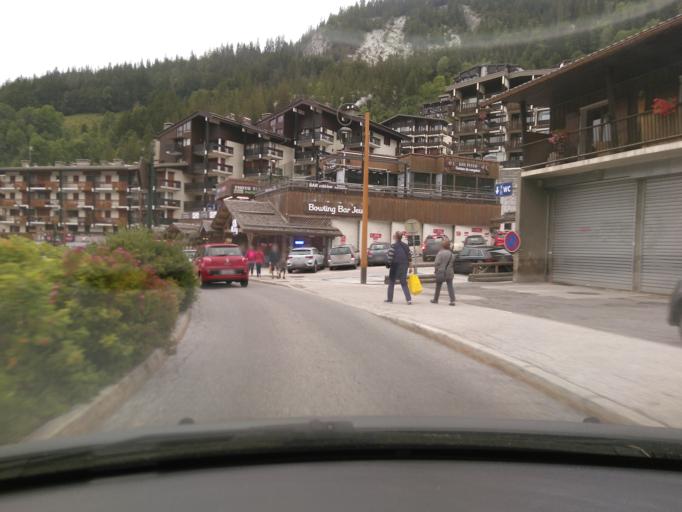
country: FR
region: Rhone-Alpes
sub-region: Departement de la Haute-Savoie
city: La Clusaz
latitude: 45.9063
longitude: 6.4303
